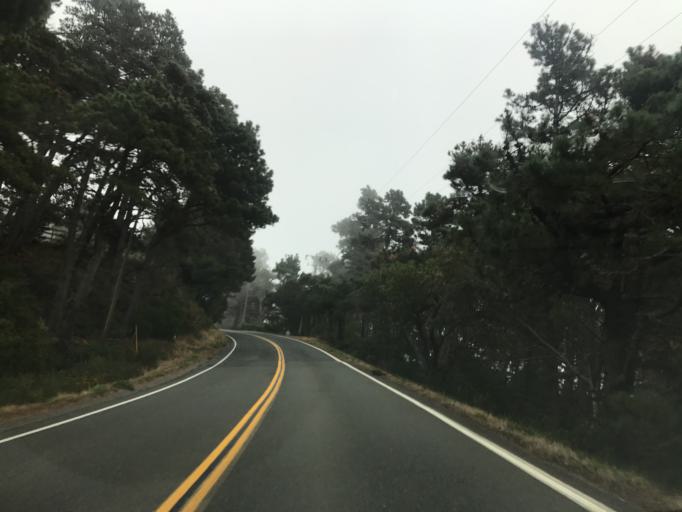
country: US
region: California
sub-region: Sonoma County
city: Sea Ranch
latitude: 38.8260
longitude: -123.6092
